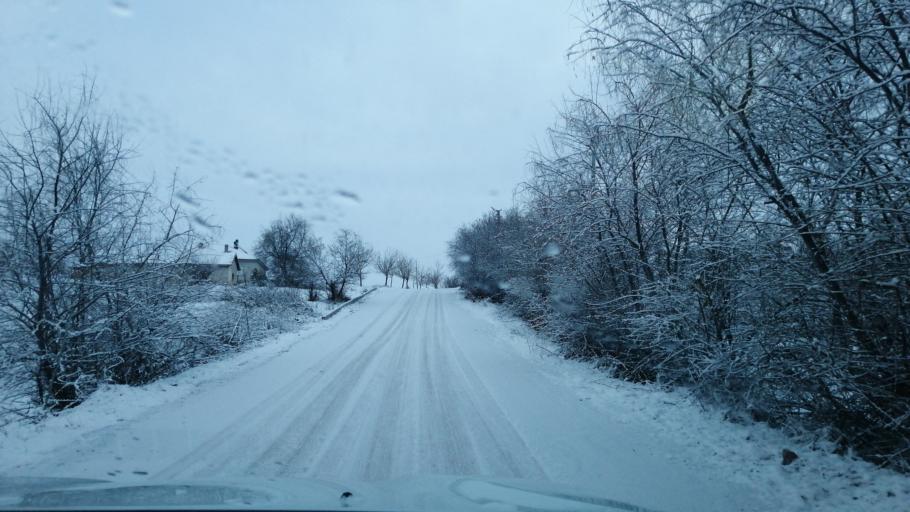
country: TR
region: Aksaray
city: Agacoren
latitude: 38.9304
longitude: 33.9524
